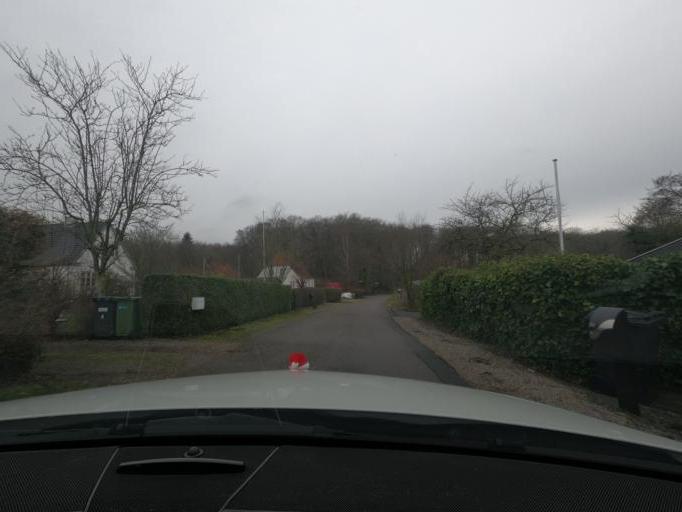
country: DK
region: South Denmark
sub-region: Haderslev Kommune
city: Starup
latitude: 55.1929
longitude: 9.5804
